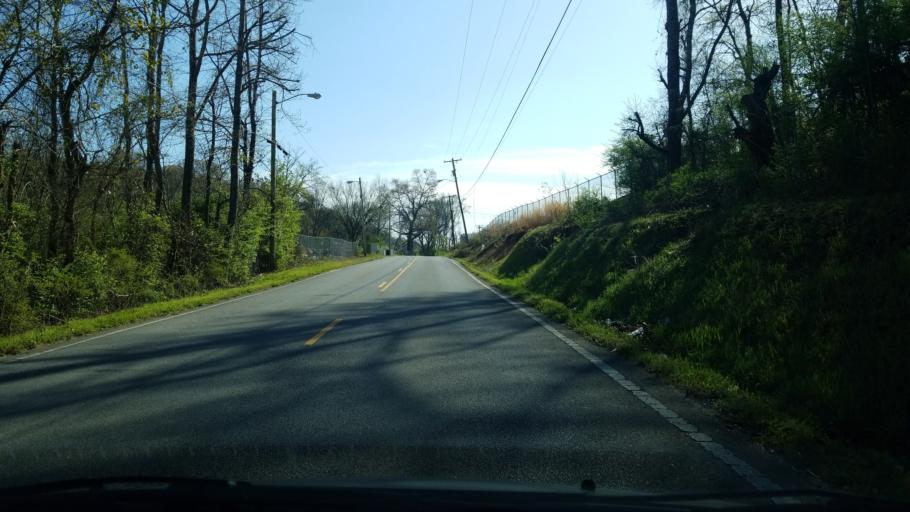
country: US
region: Tennessee
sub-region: Hamilton County
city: East Chattanooga
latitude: 35.0682
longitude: -85.2245
